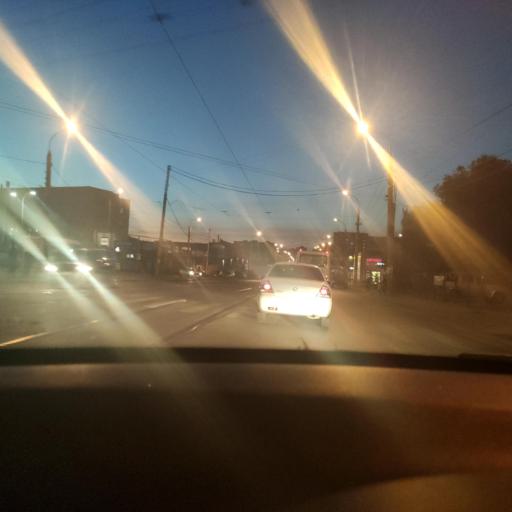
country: RU
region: Samara
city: Samara
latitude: 53.1918
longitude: 50.1685
